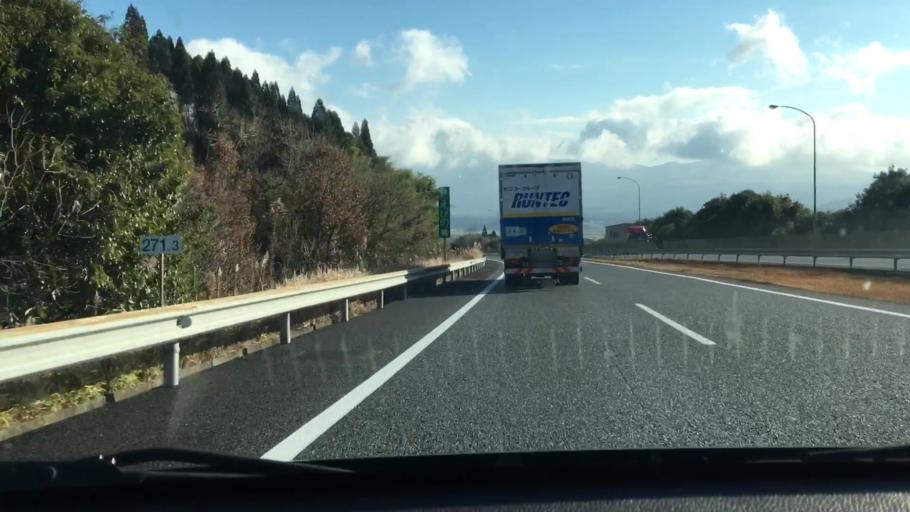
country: JP
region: Kumamoto
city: Hitoyoshi
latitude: 32.0733
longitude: 130.7933
